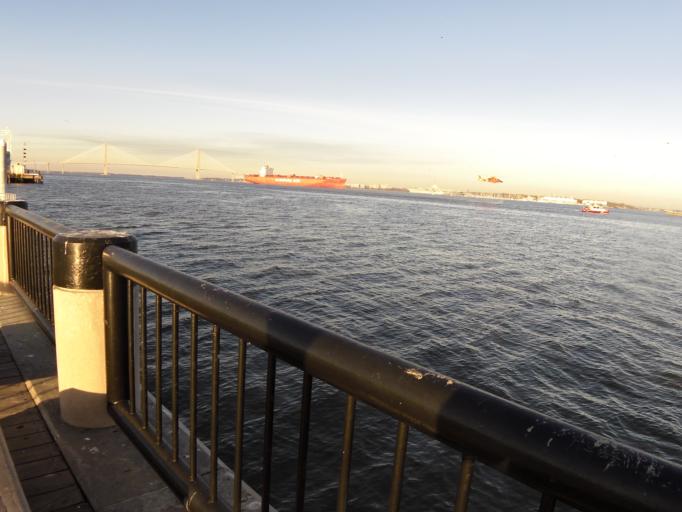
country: US
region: South Carolina
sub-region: Charleston County
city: Charleston
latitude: 32.7795
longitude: -79.9237
